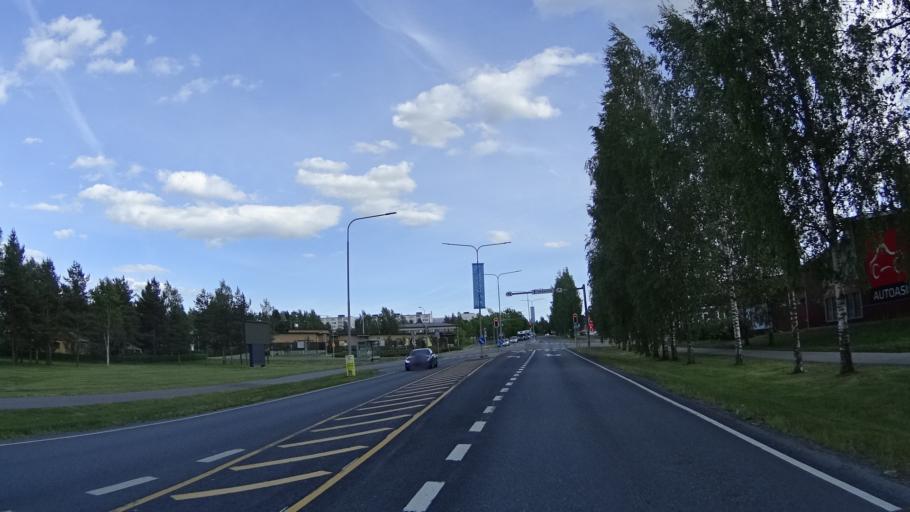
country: FI
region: Haeme
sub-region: Forssa
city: Forssa
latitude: 60.8227
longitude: 23.6290
